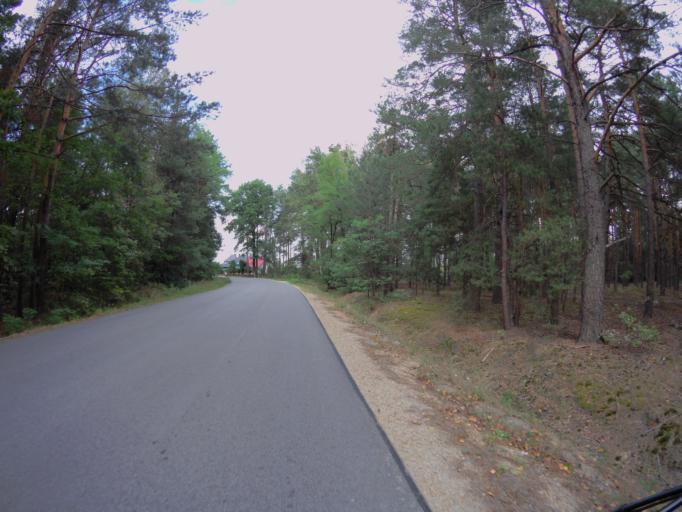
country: PL
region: Subcarpathian Voivodeship
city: Nowa Sarzyna
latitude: 50.2800
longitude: 22.3529
